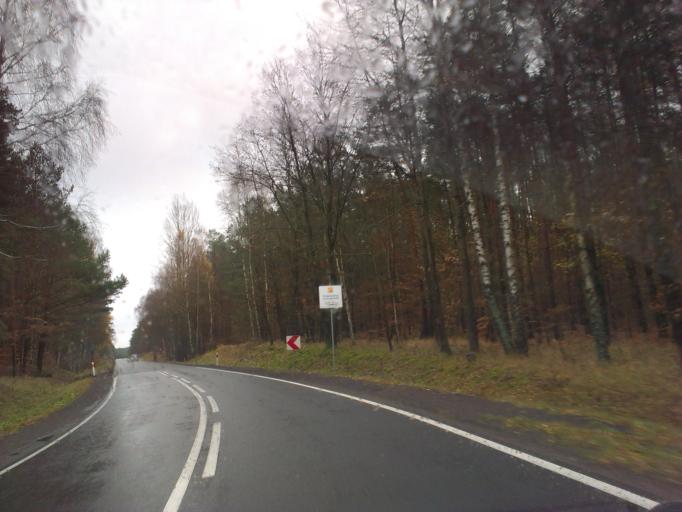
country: PL
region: West Pomeranian Voivodeship
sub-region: Powiat szczecinecki
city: Lubowo
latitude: 53.5971
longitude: 16.4276
